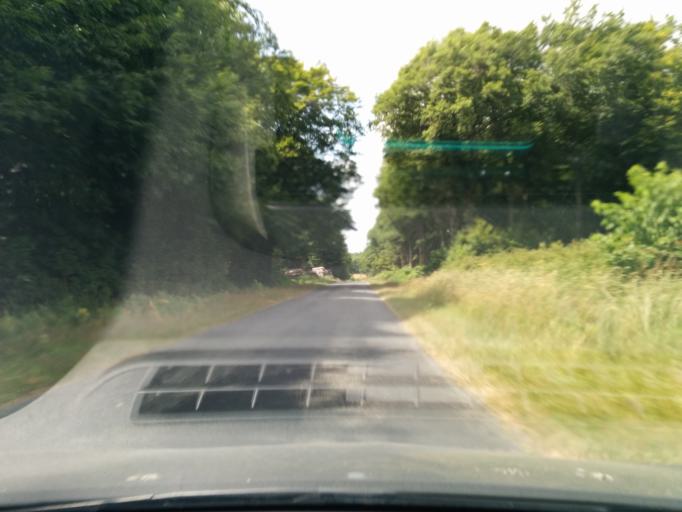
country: FR
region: Centre
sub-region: Departement du Cher
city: Henrichemont
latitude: 47.3488
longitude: 2.6237
